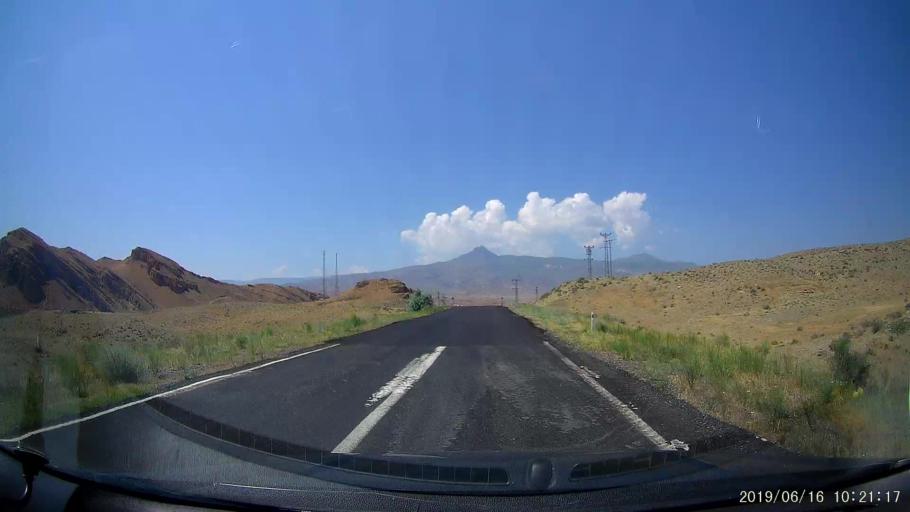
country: TR
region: Igdir
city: Tuzluca
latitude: 40.1388
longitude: 43.6386
